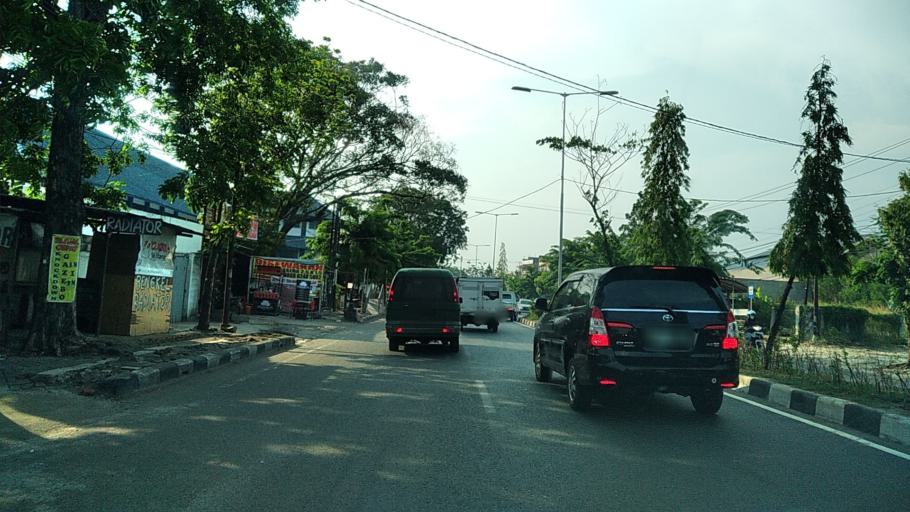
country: ID
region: Central Java
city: Semarang
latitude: -6.9964
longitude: 110.4625
